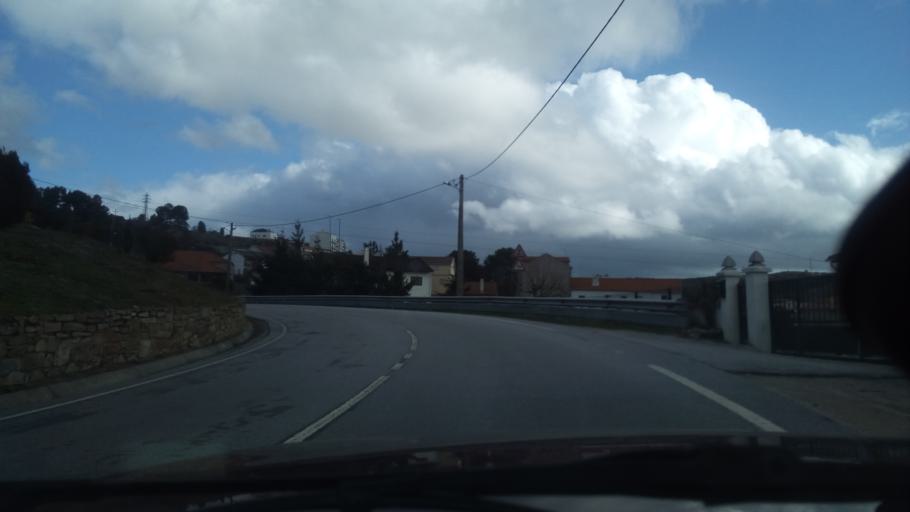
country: PT
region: Guarda
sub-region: Guarda
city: Guarda
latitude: 40.5420
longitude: -7.2974
